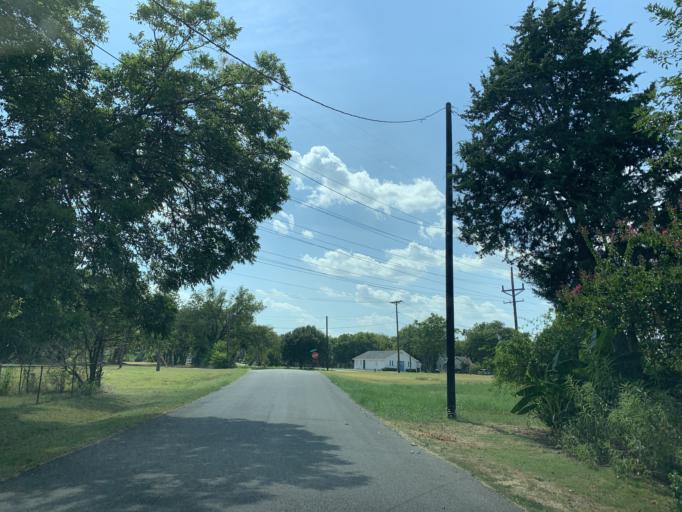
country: US
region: Texas
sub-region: Dallas County
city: Hutchins
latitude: 32.7063
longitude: -96.7661
